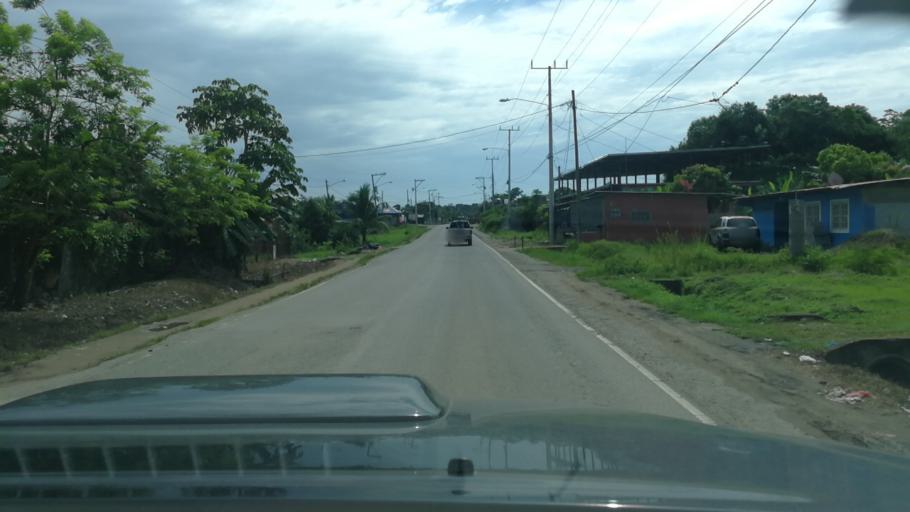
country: PA
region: Panama
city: Paso Blanco
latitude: 9.1199
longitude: -79.2561
